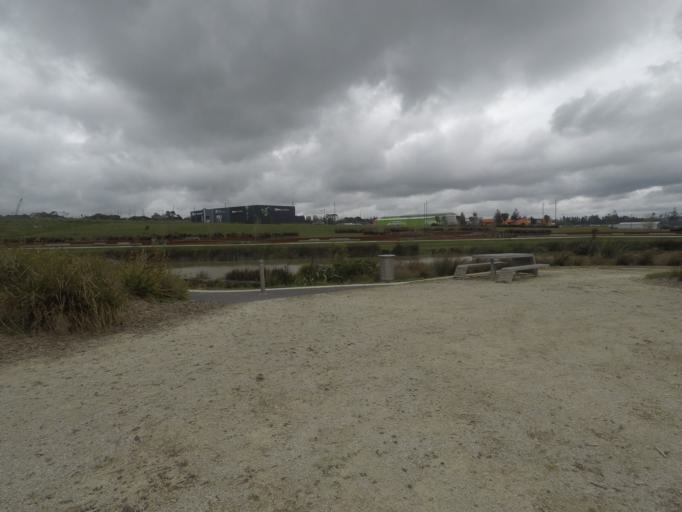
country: NZ
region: Auckland
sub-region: Auckland
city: Rosebank
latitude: -36.8126
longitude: 174.6068
